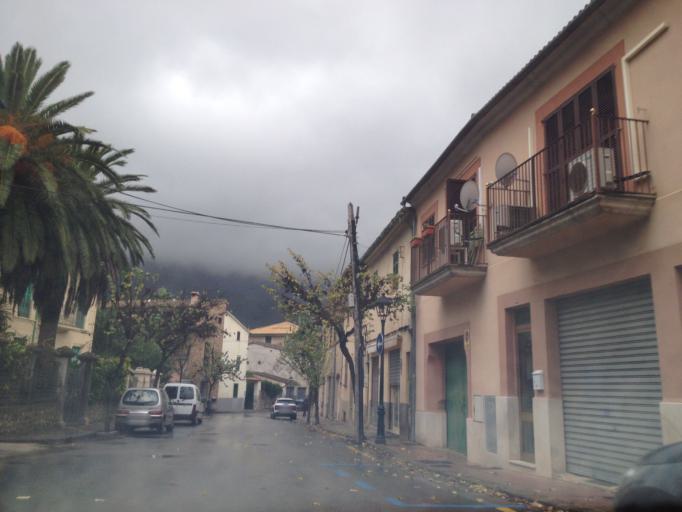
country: ES
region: Balearic Islands
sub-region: Illes Balears
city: Soller
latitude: 39.7711
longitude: 2.7170
